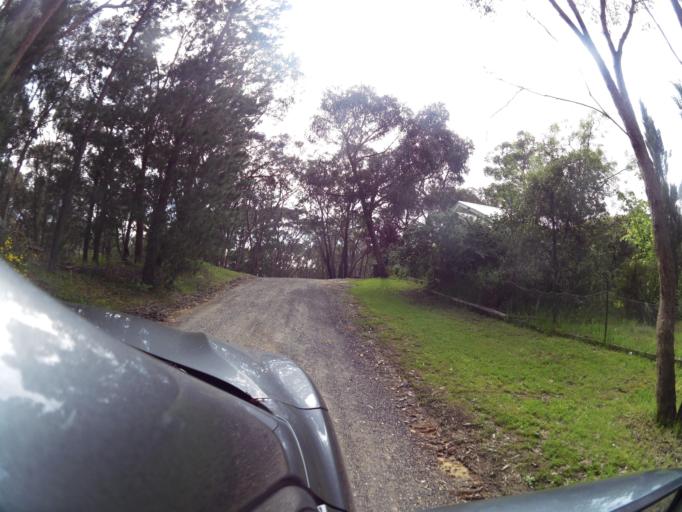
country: AU
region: Victoria
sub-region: Mount Alexander
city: Castlemaine
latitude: -37.3065
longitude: 144.1427
